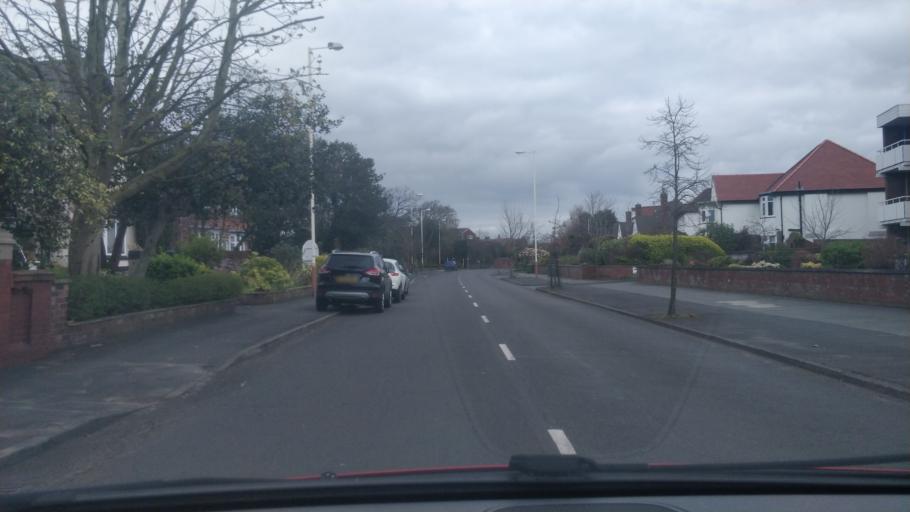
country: GB
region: England
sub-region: Sefton
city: Southport
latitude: 53.6406
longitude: -3.0167
